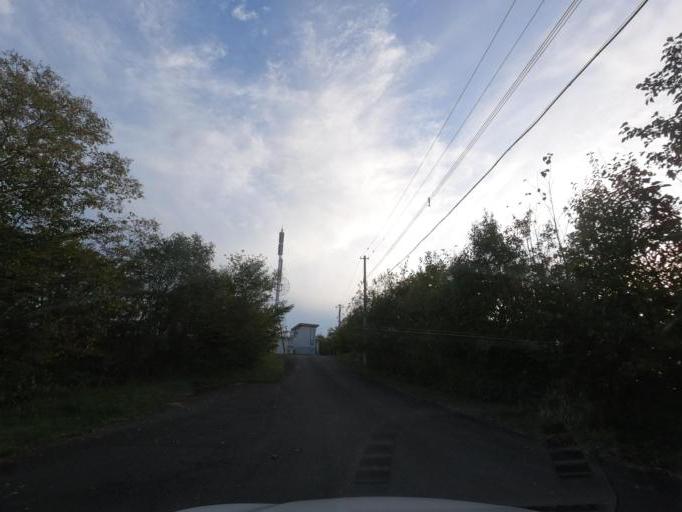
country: JP
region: Hokkaido
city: Obihiro
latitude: 42.5833
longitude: 143.3141
